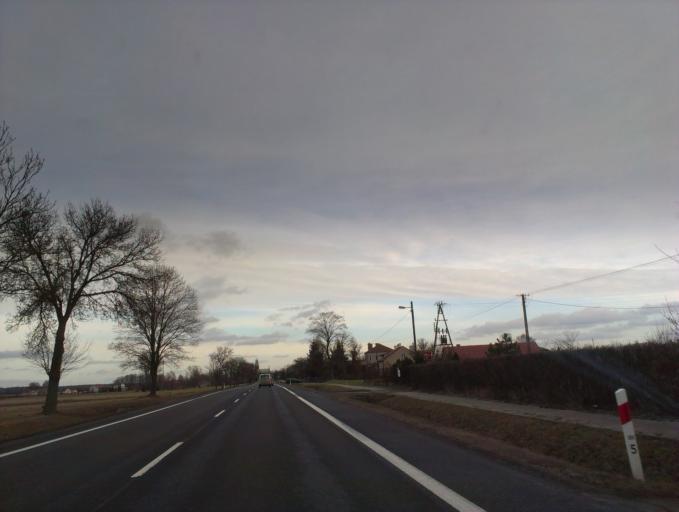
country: PL
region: Masovian Voivodeship
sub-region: Powiat sierpecki
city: Szczutowo
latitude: 52.9026
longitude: 19.5113
